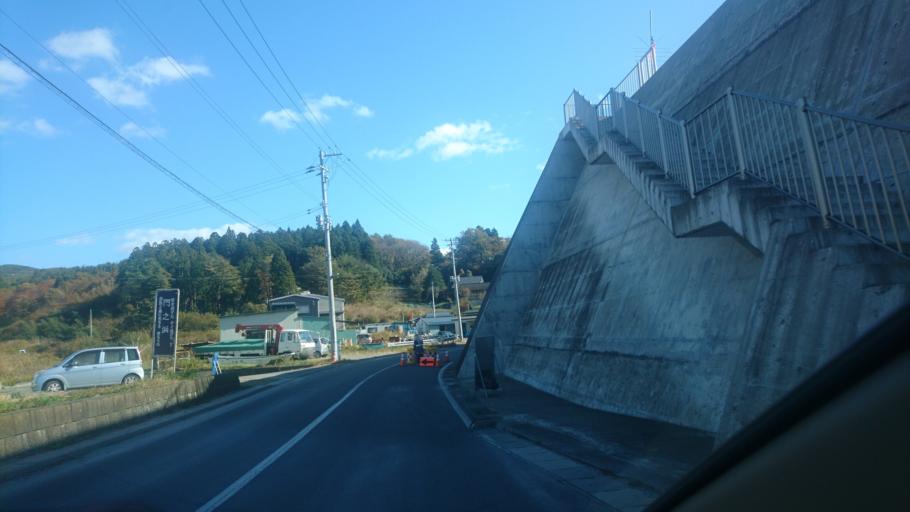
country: JP
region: Iwate
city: Ofunato
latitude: 38.9979
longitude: 141.7194
